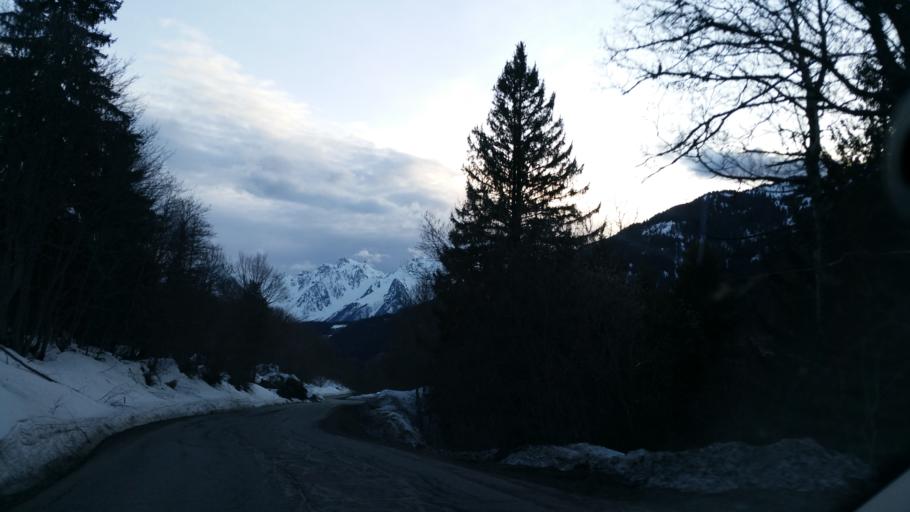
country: FR
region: Rhone-Alpes
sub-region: Departement de la Savoie
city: La Chambre
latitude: 45.4143
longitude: 6.3554
